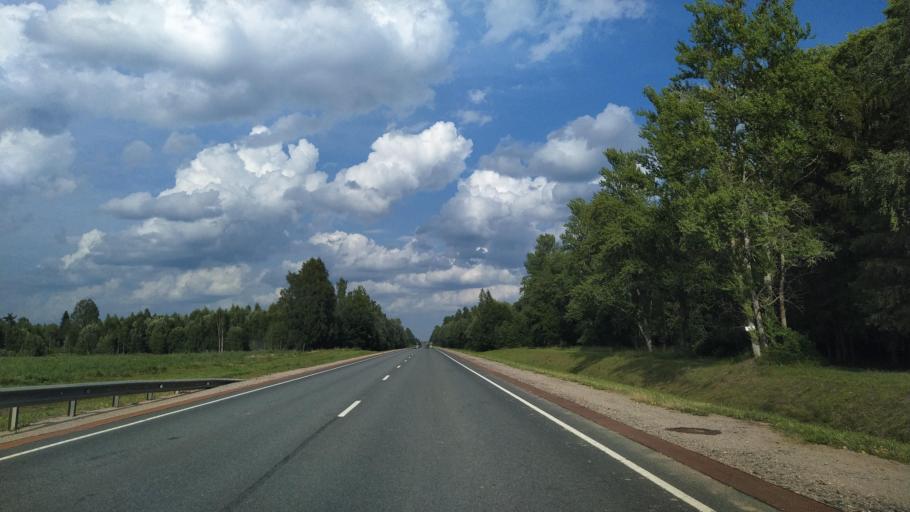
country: RU
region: Novgorod
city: Shimsk
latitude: 58.1836
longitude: 30.5461
